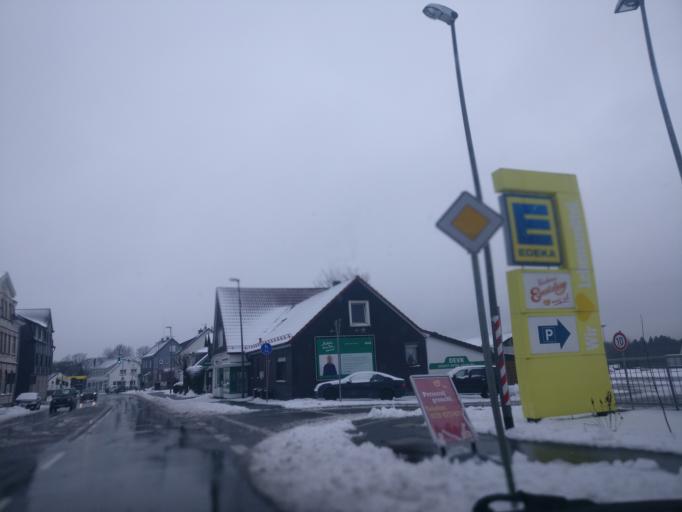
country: DE
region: North Rhine-Westphalia
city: Radevormwald
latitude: 51.2020
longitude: 7.3335
